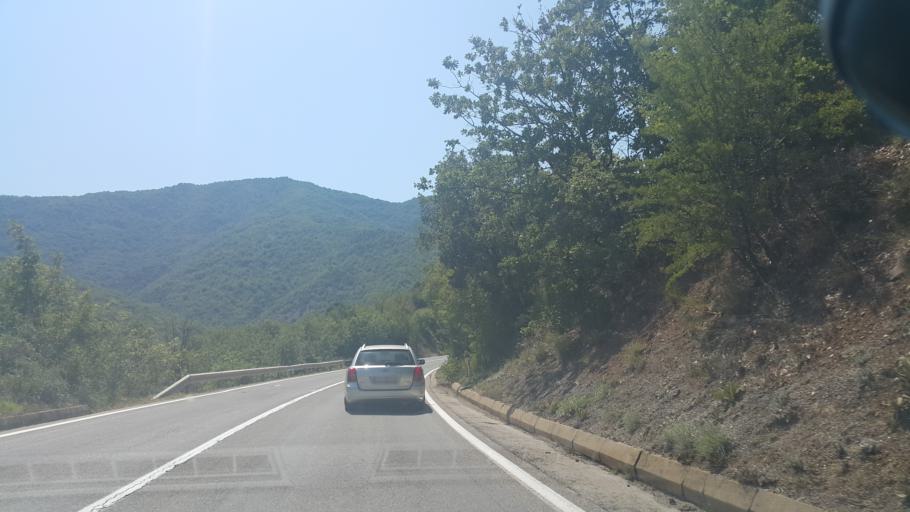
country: MK
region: Gevgelija
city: Miravci
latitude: 41.3863
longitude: 22.3656
